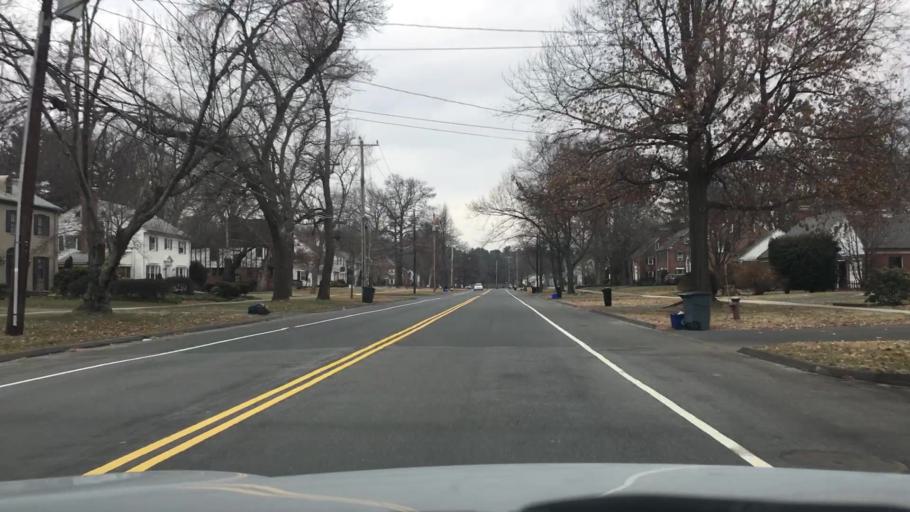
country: US
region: Massachusetts
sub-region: Hampden County
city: Longmeadow
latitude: 42.0534
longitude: -72.5726
